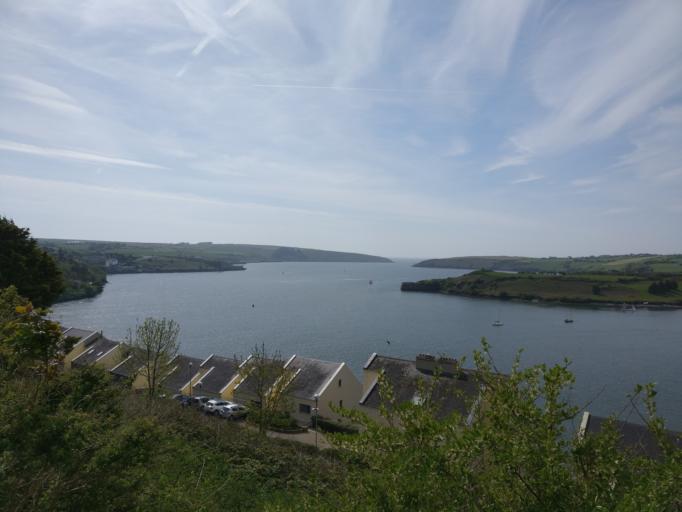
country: IE
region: Munster
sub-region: County Cork
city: Kinsale
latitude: 51.7062
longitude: -8.5112
